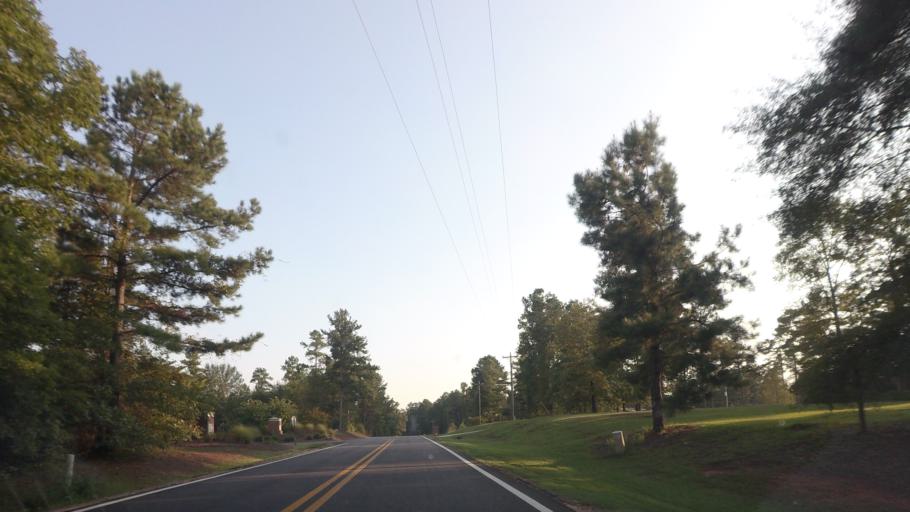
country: US
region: Georgia
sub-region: Bibb County
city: West Point
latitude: 32.9072
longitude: -83.8224
